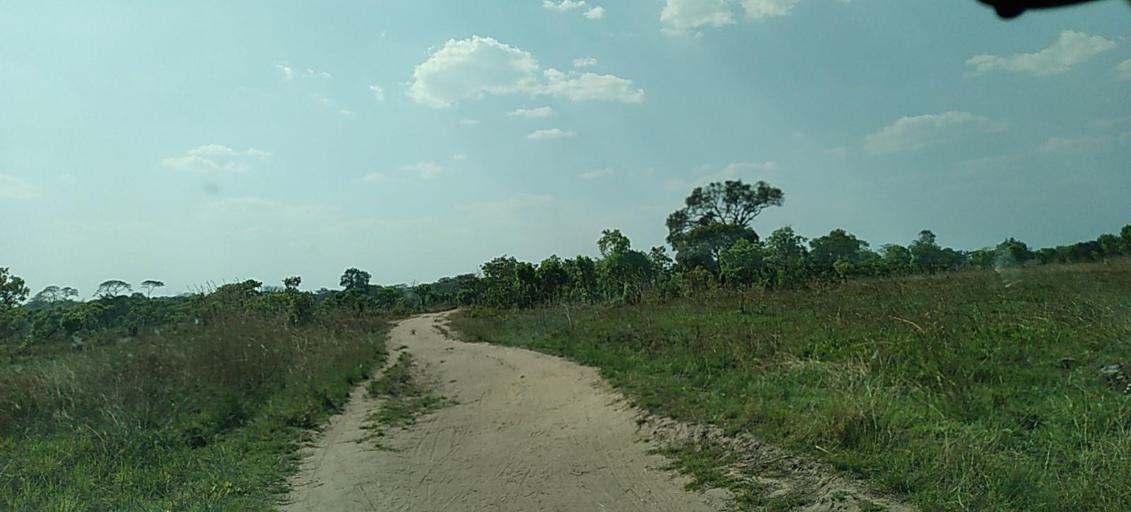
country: ZM
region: North-Western
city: Kalengwa
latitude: -13.1141
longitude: 24.9936
